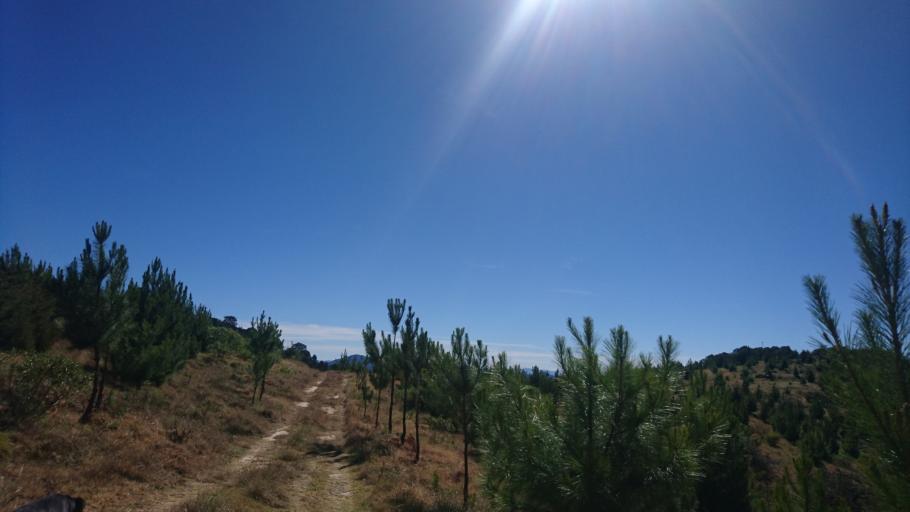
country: MX
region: San Luis Potosi
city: Zaragoza
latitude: 22.0160
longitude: -100.6212
